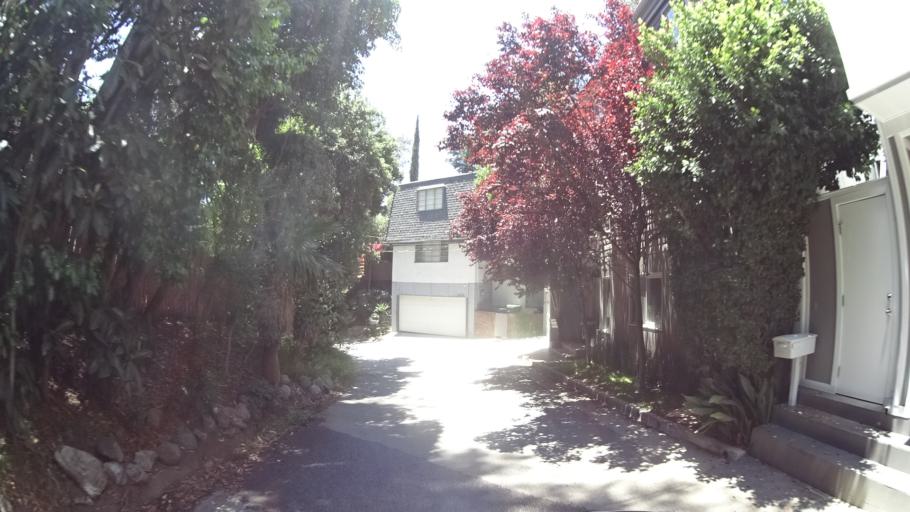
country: US
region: California
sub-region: Los Angeles County
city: Universal City
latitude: 34.1175
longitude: -118.3725
